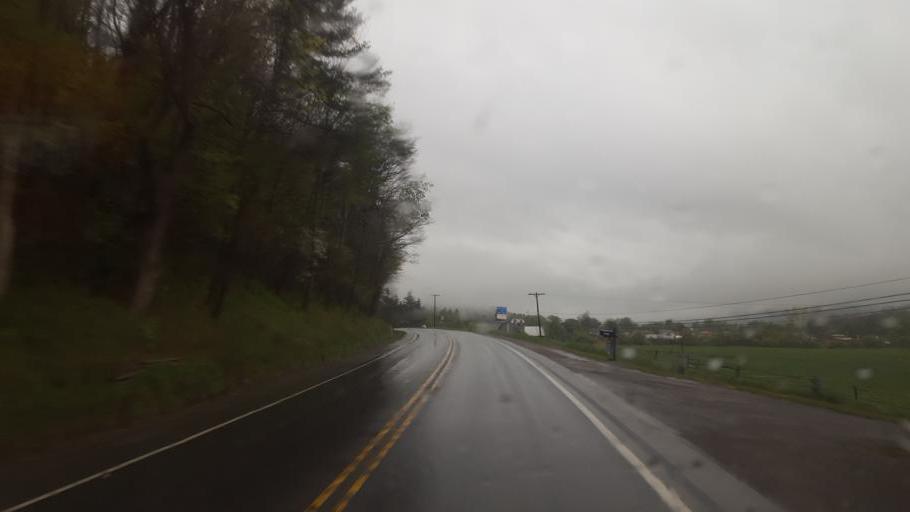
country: US
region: Pennsylvania
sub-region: Tioga County
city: Westfield
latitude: 41.9556
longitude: -77.4492
